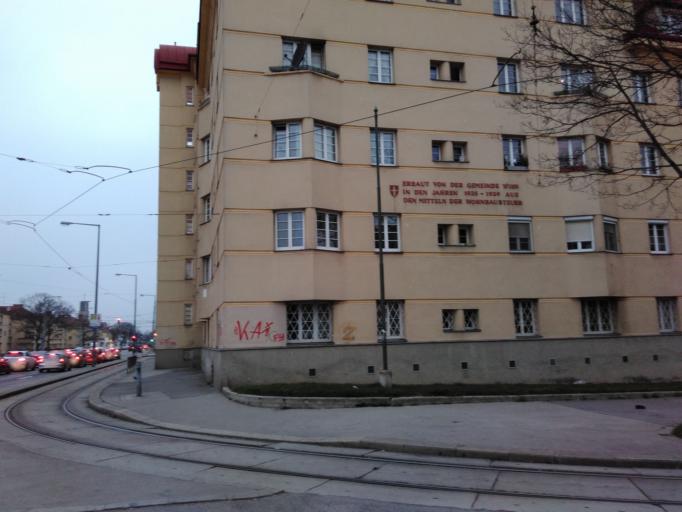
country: AT
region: Vienna
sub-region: Wien Stadt
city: Vienna
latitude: 48.1656
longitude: 16.3652
